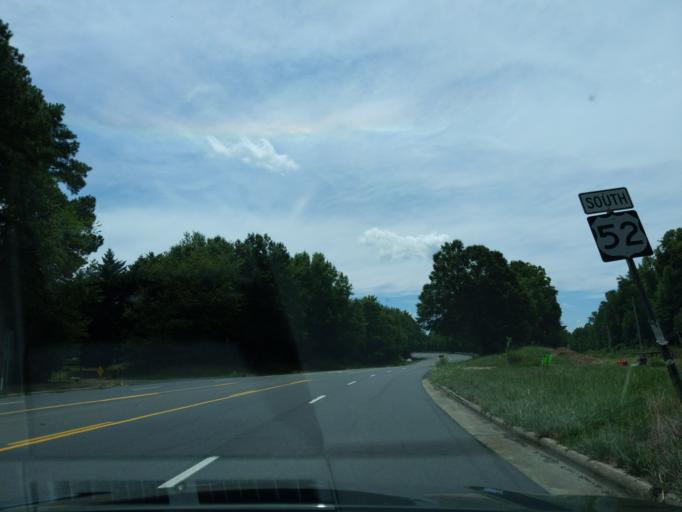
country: US
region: North Carolina
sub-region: Stanly County
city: Albemarle
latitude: 35.4432
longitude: -80.2223
